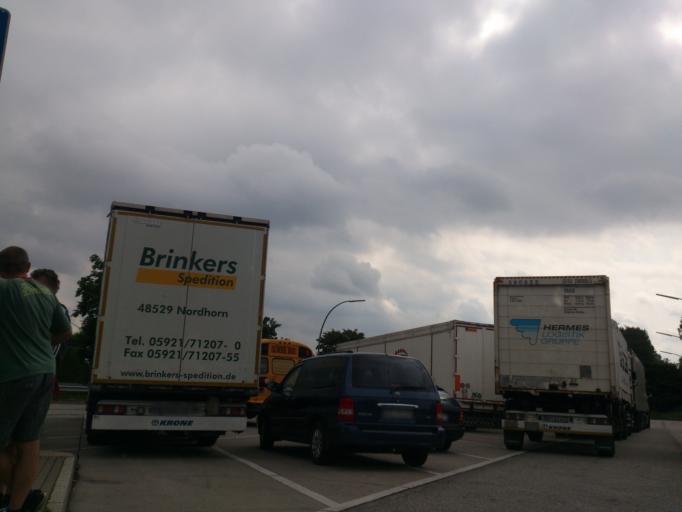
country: DE
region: Lower Saxony
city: Seevetal
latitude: 53.4240
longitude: 9.9637
